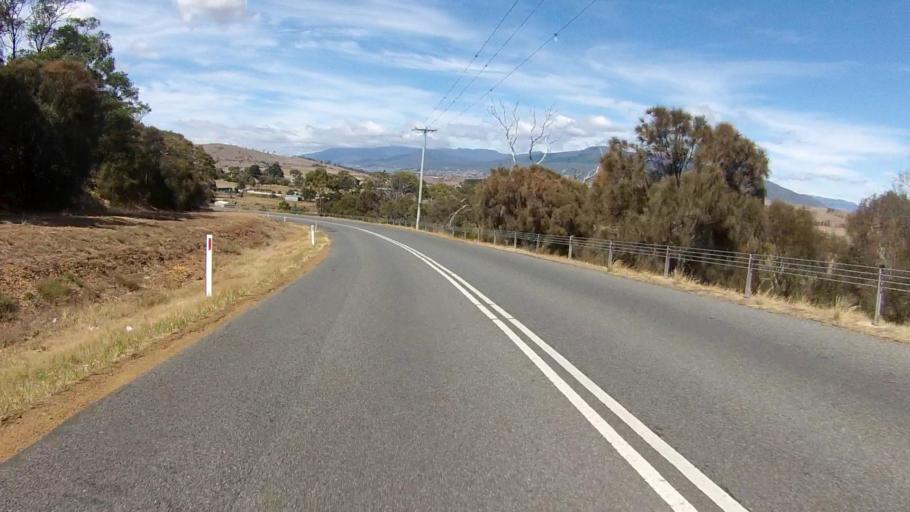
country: AU
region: Tasmania
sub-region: Brighton
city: Bridgewater
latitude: -42.7085
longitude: 147.2691
